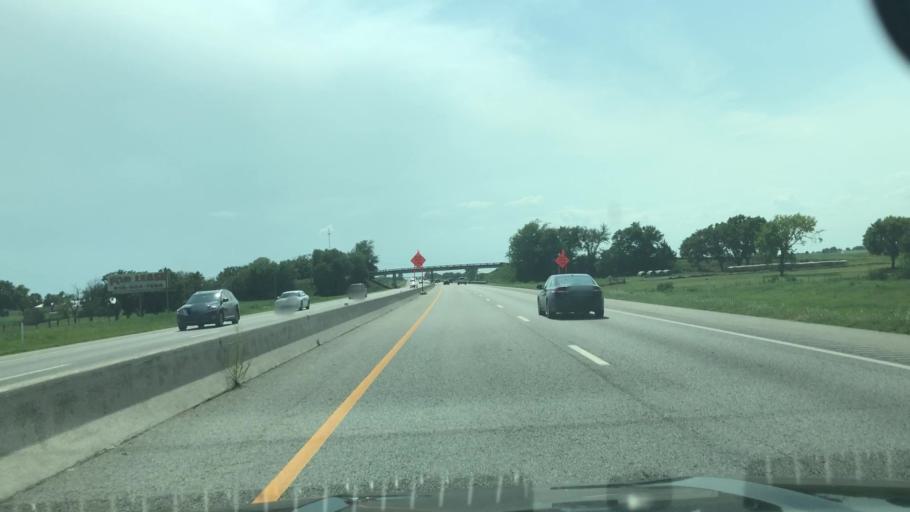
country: US
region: Oklahoma
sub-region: Ottawa County
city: Afton
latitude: 36.7069
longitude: -94.9786
